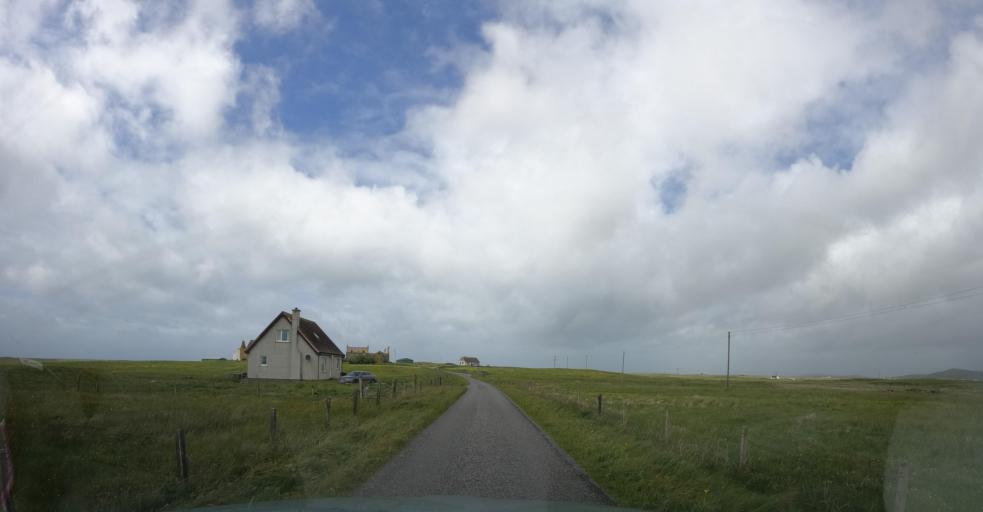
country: GB
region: Scotland
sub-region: Eilean Siar
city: Isle of South Uist
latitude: 57.2592
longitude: -7.4060
